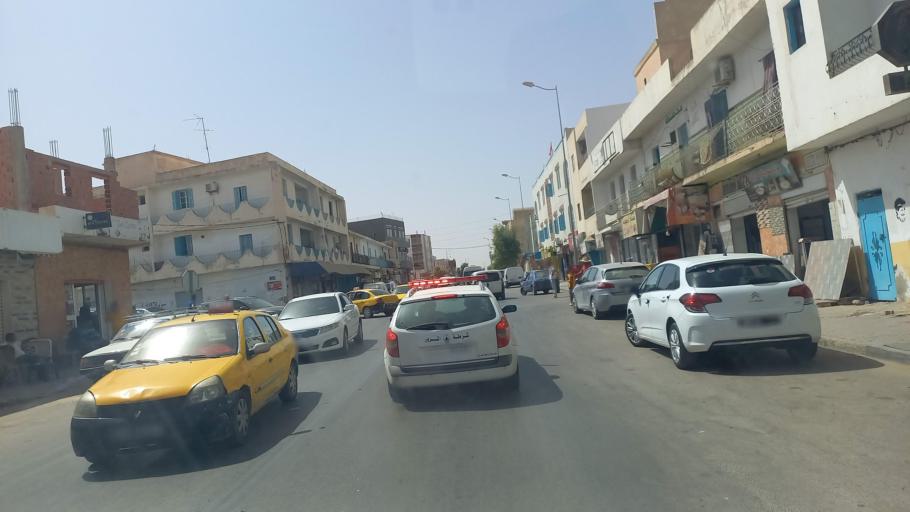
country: TN
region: Madanin
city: Medenine
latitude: 33.3340
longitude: 10.4855
